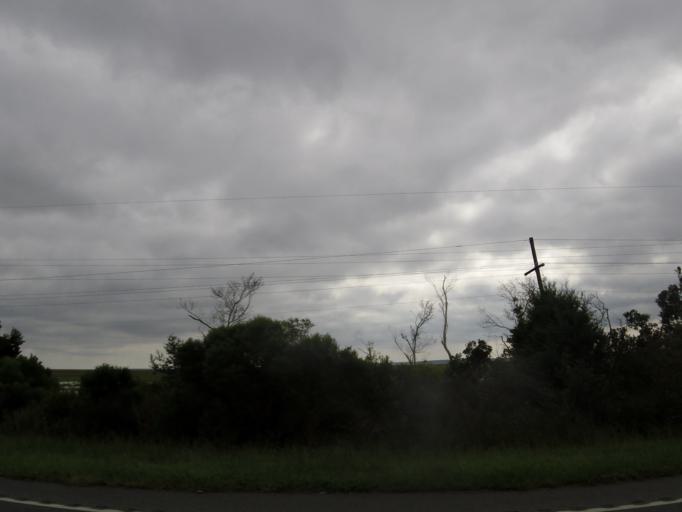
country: US
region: Georgia
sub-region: Glynn County
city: Brunswick
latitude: 31.0745
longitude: -81.4671
